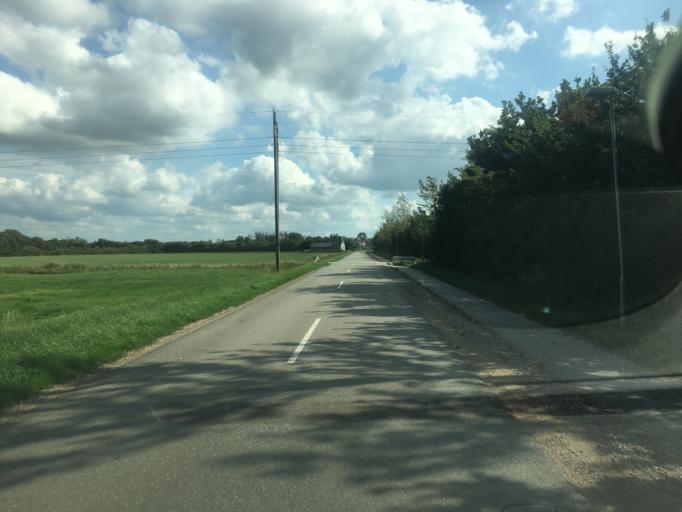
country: DE
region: Schleswig-Holstein
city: Ellhoft
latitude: 54.9448
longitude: 8.9668
